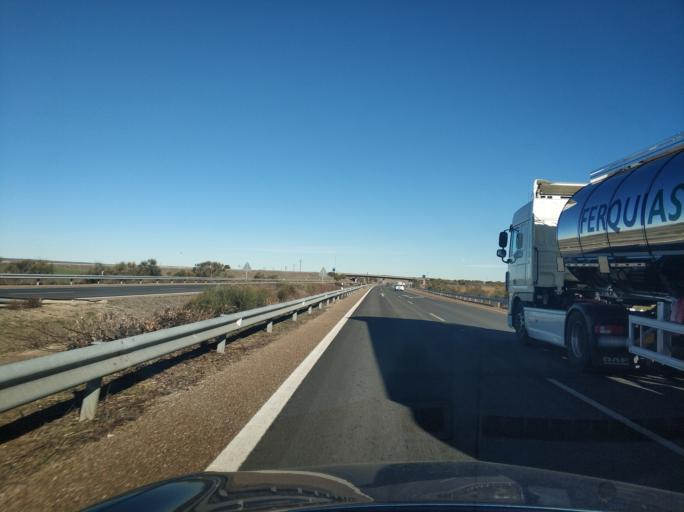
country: ES
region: Castille and Leon
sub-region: Provincia de Salamanca
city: Pajares de la Laguna
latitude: 41.0885
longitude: -5.5036
